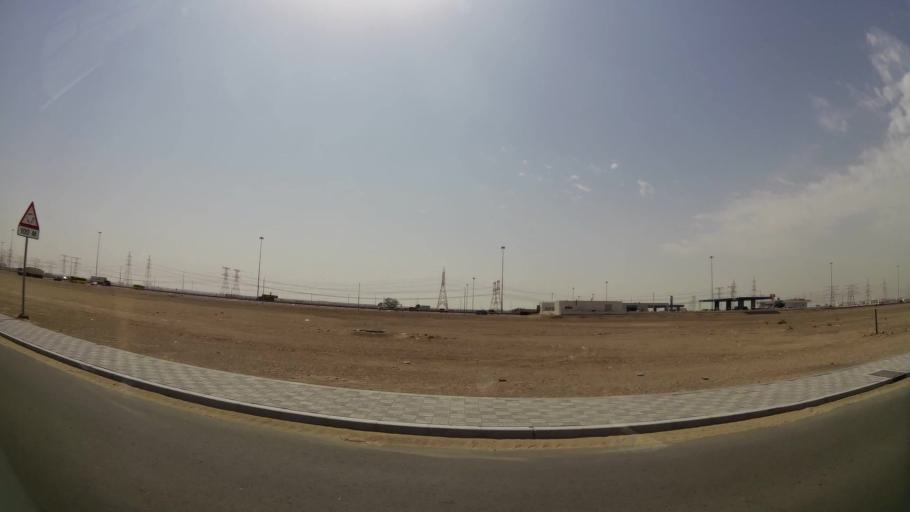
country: AE
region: Abu Dhabi
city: Abu Dhabi
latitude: 24.3053
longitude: 54.5352
